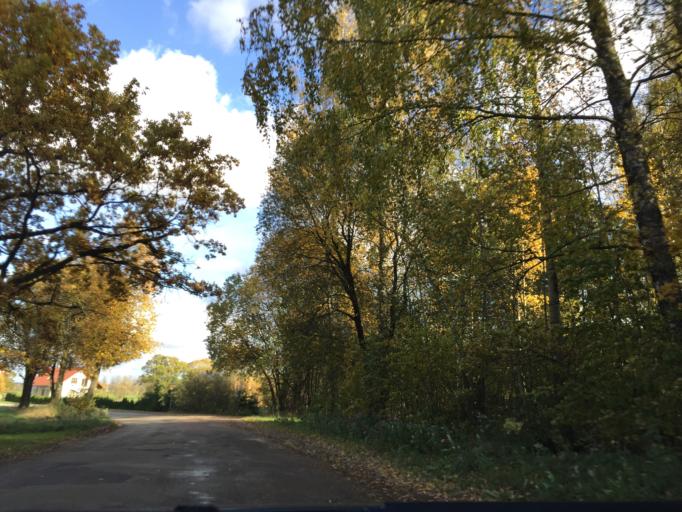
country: LV
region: Lielvarde
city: Lielvarde
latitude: 56.7156
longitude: 24.8571
